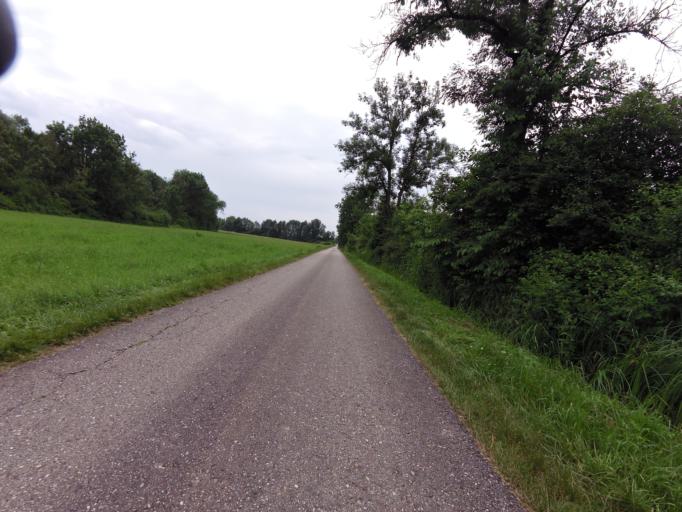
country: DE
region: Bavaria
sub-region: Upper Bavaria
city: Wang
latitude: 48.4823
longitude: 11.9699
